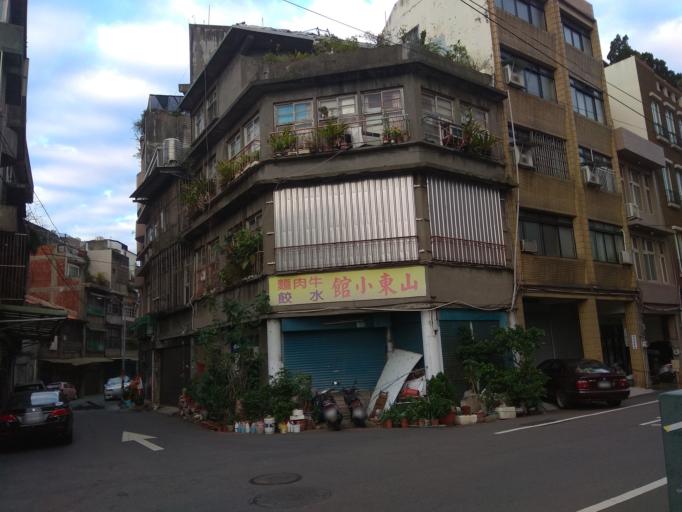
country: TW
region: Taiwan
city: Taoyuan City
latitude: 24.9967
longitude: 121.3070
